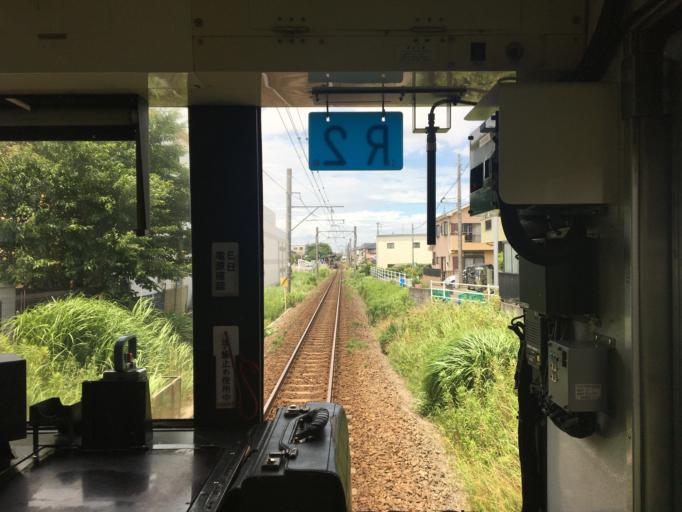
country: JP
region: Kanagawa
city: Chigasaki
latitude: 35.3545
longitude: 139.4003
